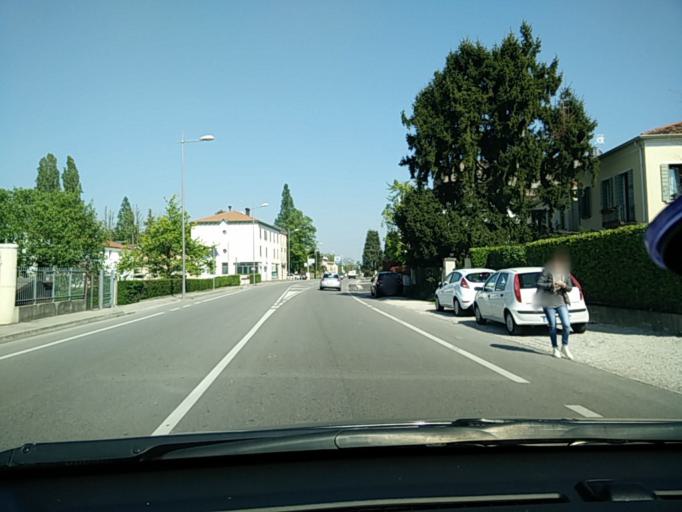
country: IT
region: Veneto
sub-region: Provincia di Venezia
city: Fiesso
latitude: 45.4167
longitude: 12.0342
